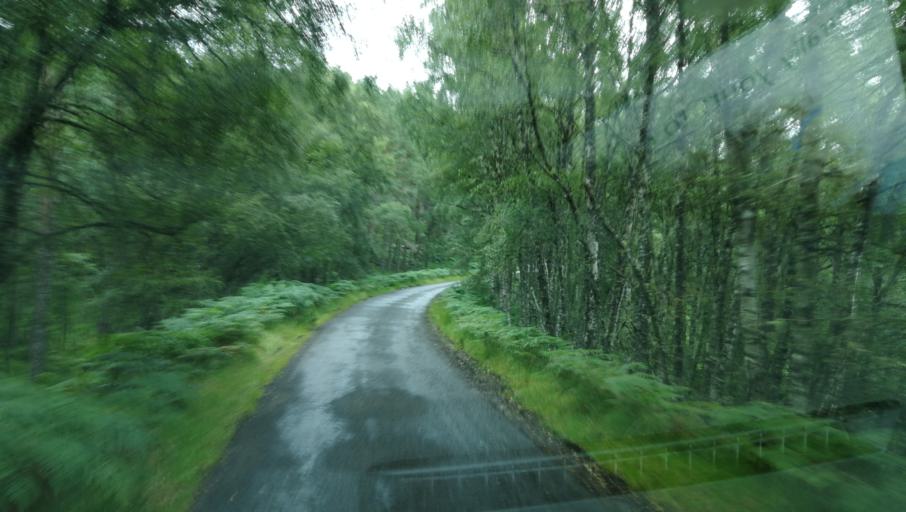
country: GB
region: Scotland
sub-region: Highland
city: Spean Bridge
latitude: 57.2997
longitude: -4.8979
